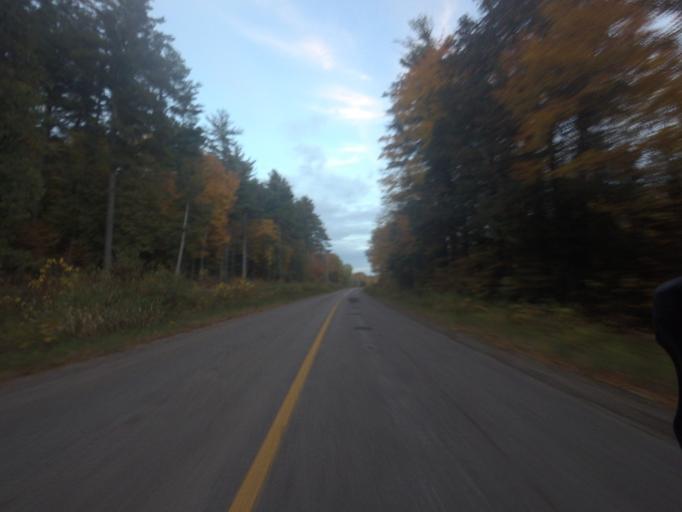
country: CA
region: Ontario
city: Renfrew
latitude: 45.3544
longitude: -76.9532
